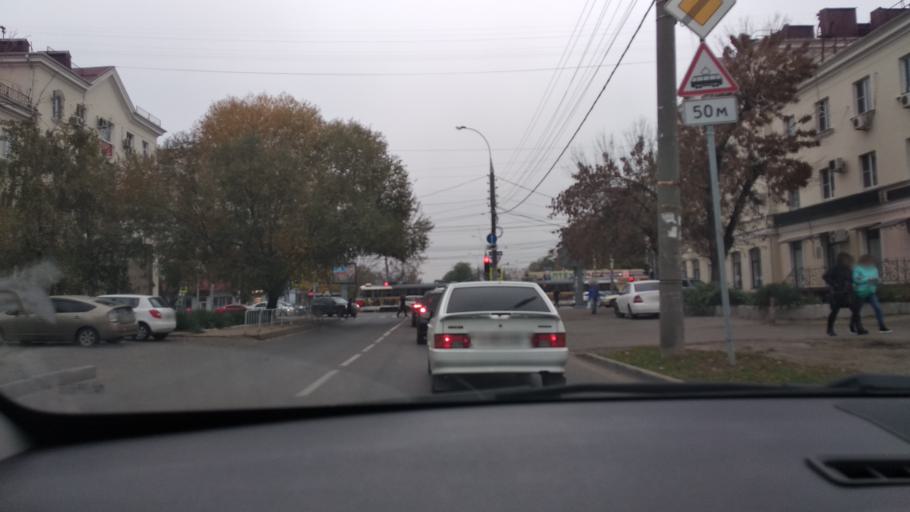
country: RU
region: Krasnodarskiy
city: Krasnodar
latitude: 45.0215
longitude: 39.0098
